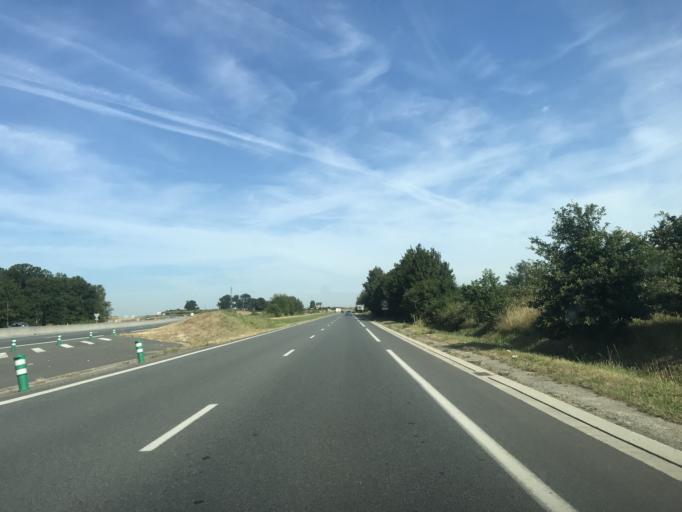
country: FR
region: Haute-Normandie
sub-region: Departement de la Seine-Maritime
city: Roumare
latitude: 49.5227
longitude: 0.9698
